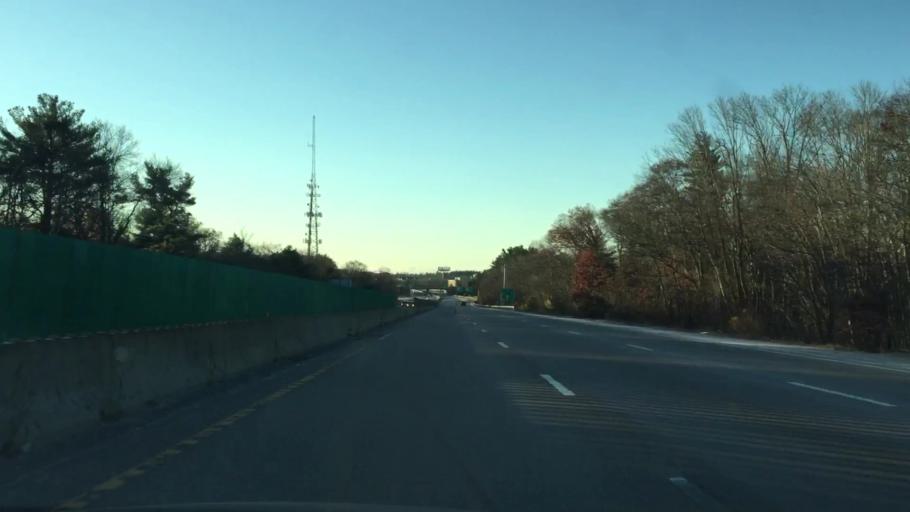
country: US
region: Massachusetts
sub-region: Plymouth County
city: Brockton
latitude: 42.0697
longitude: -71.0624
